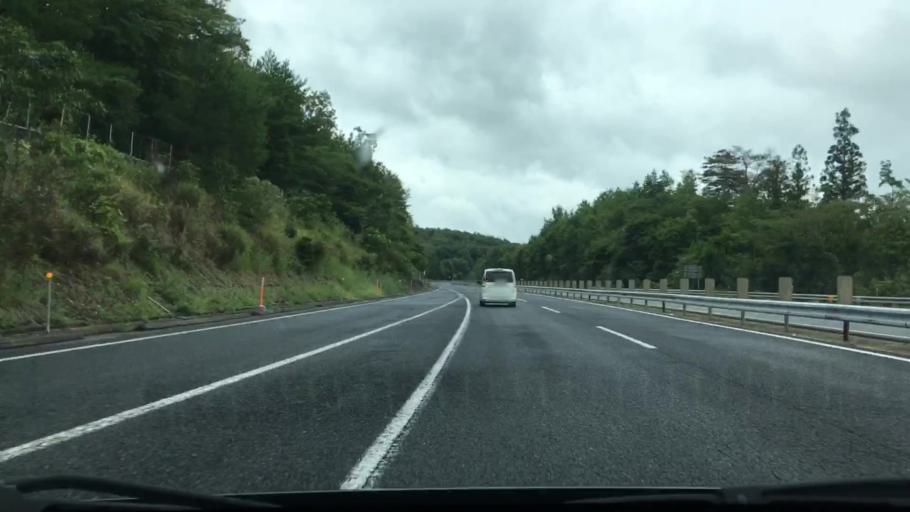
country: JP
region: Hiroshima
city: Miyoshi
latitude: 34.7486
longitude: 132.7238
